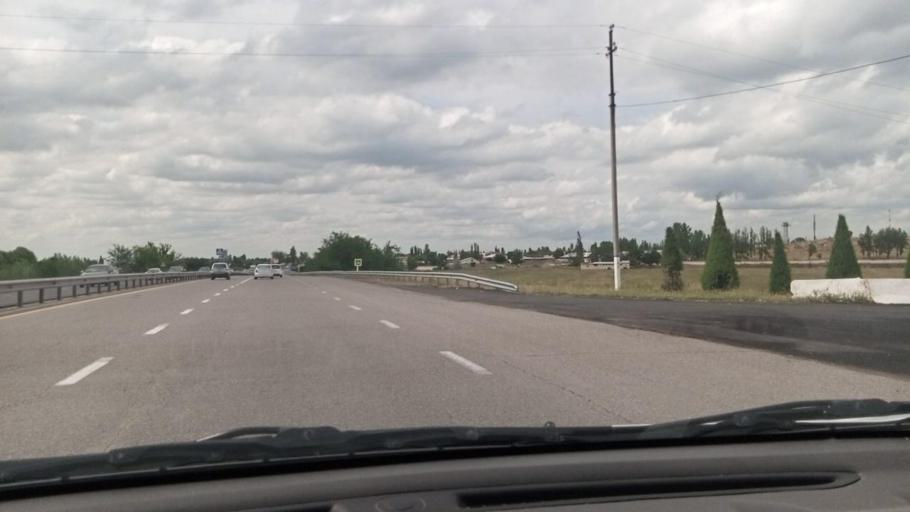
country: UZ
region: Toshkent
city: Tuytepa
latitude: 41.1228
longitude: 69.4404
